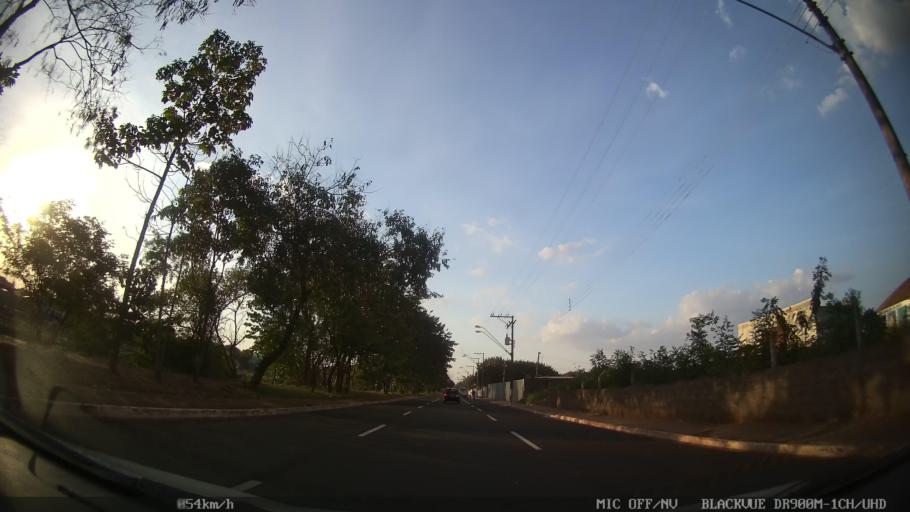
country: BR
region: Sao Paulo
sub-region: Ribeirao Preto
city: Ribeirao Preto
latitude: -21.1310
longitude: -47.8031
